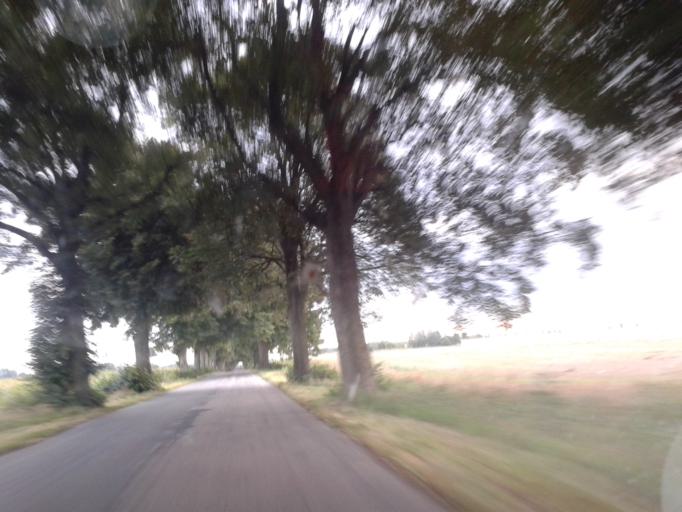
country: PL
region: West Pomeranian Voivodeship
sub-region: Powiat szczecinecki
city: Grzmiaca
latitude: 53.8457
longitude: 16.4513
